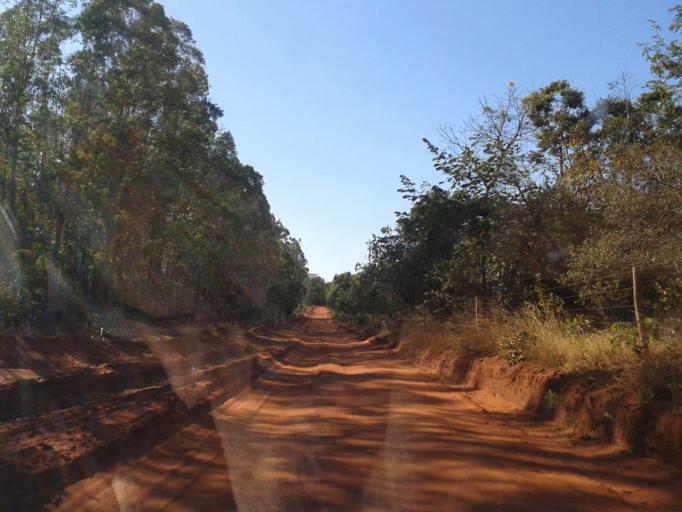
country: BR
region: Minas Gerais
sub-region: Ituiutaba
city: Ituiutaba
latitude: -19.0344
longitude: -49.3077
